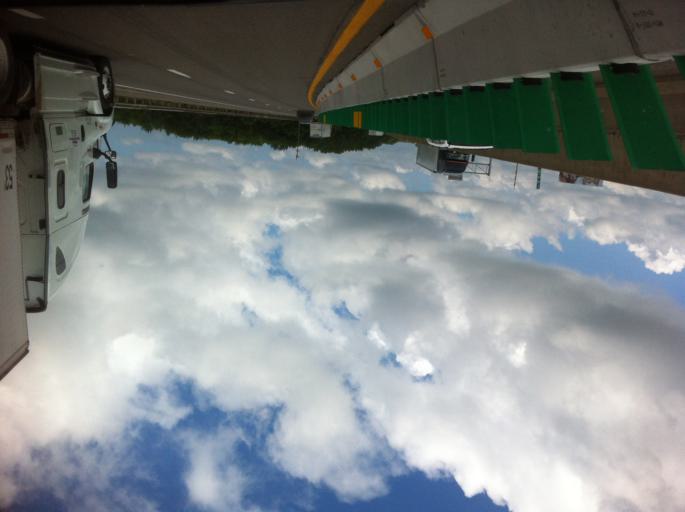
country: US
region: Ohio
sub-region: Lorain County
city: Elyria
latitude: 41.3917
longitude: -82.1222
